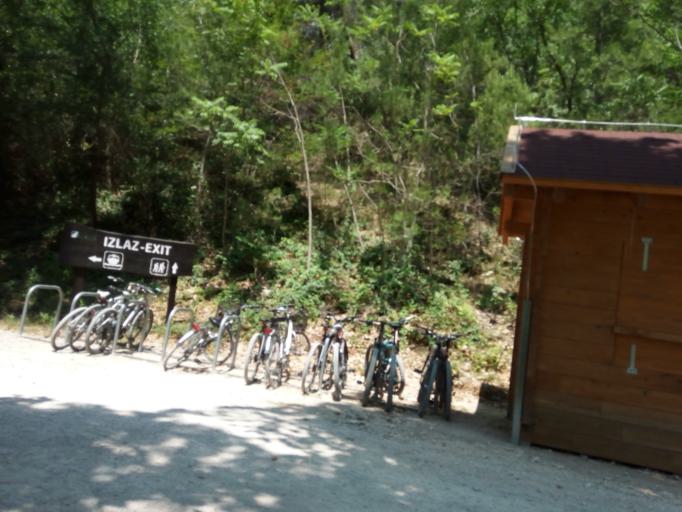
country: HR
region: Sibensko-Kniniska
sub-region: Grad Sibenik
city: Sibenik
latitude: 43.8079
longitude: 15.9621
